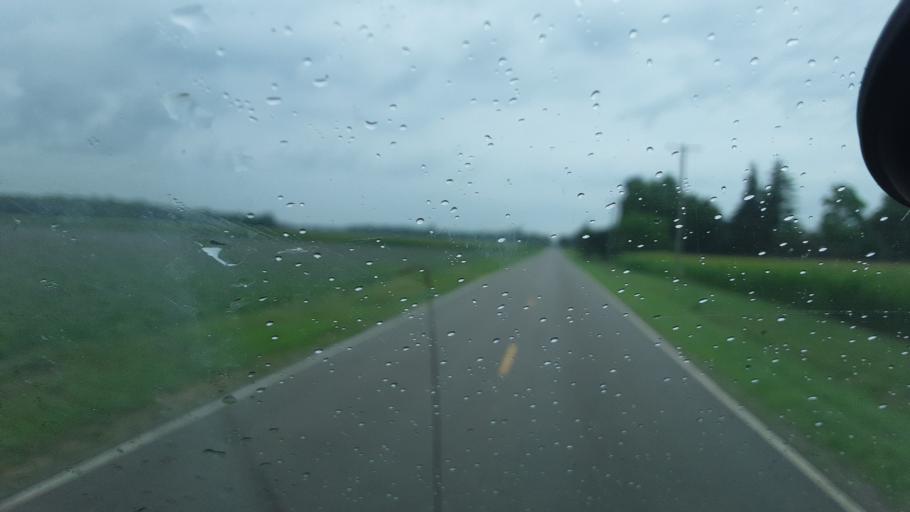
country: US
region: Ohio
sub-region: Williams County
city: Bryan
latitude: 41.3686
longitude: -84.6306
